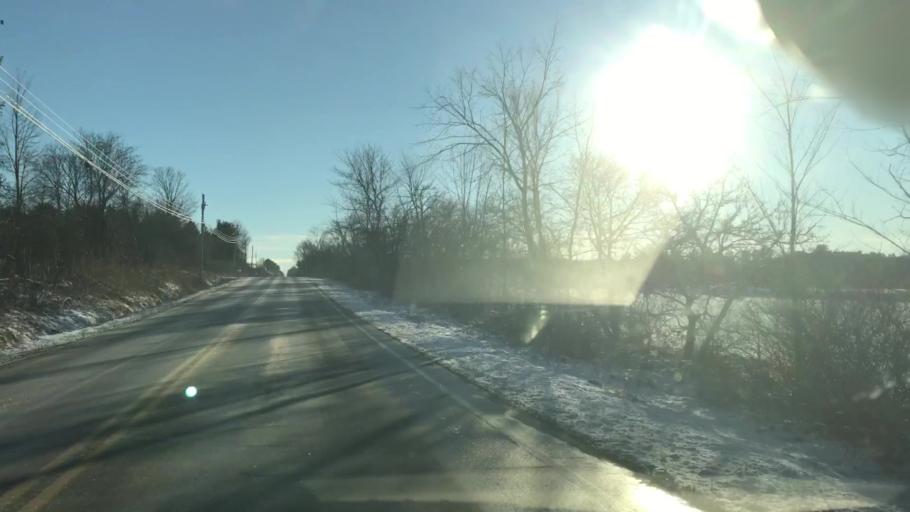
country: US
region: New Hampshire
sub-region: Grafton County
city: Haverhill
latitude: 44.0090
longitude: -72.0705
